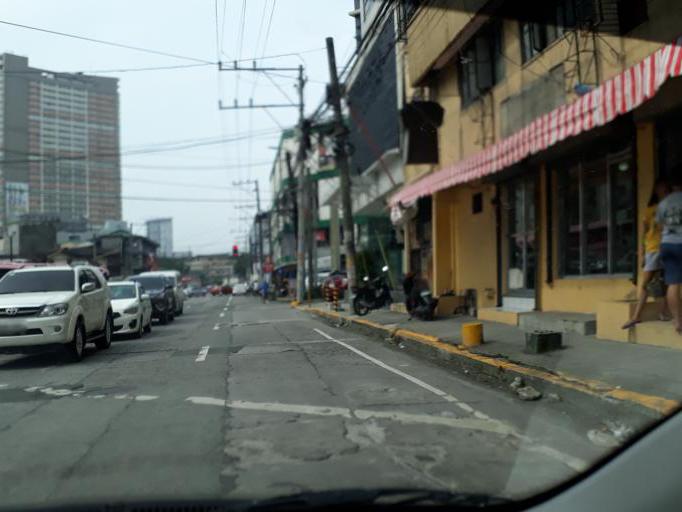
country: PH
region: Metro Manila
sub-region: City of Manila
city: Manila
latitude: 14.6070
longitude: 120.9933
